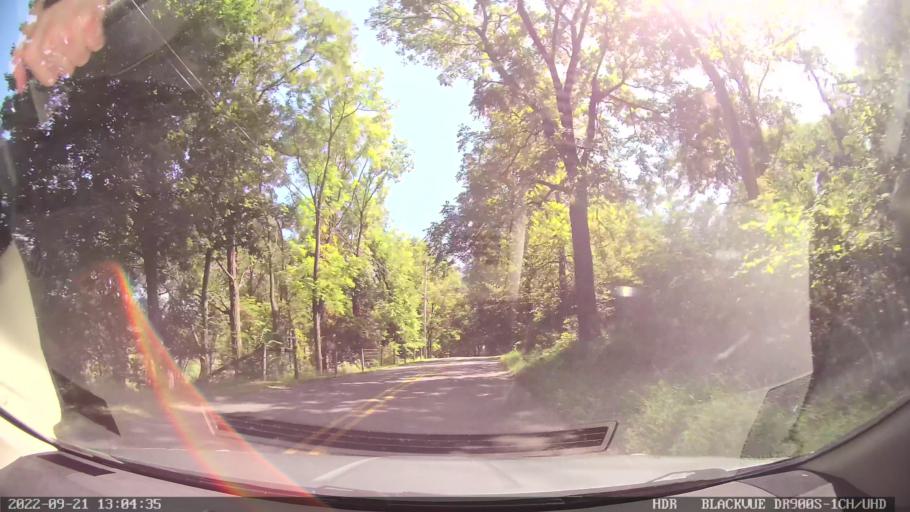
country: US
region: Pennsylvania
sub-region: Berks County
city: Kutztown
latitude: 40.4928
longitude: -75.7463
